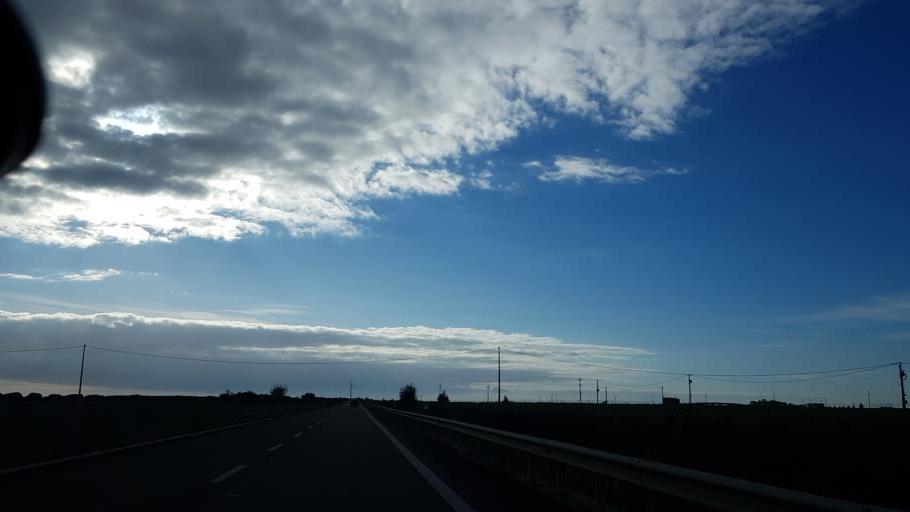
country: IT
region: Apulia
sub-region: Provincia di Brindisi
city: La Rosa
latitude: 40.5884
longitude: 17.9737
